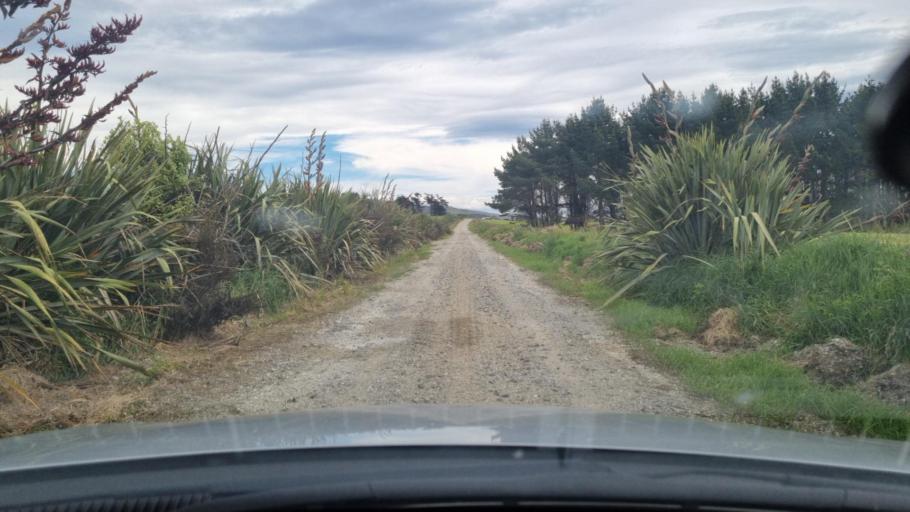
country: NZ
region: Southland
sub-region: Invercargill City
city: Bluff
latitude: -46.5201
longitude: 168.3000
